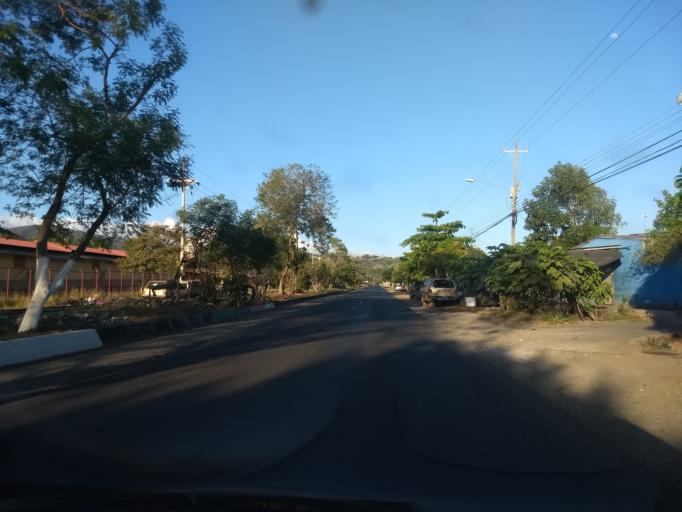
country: CR
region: Puntarenas
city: Esparza
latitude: 9.9861
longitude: -84.7167
